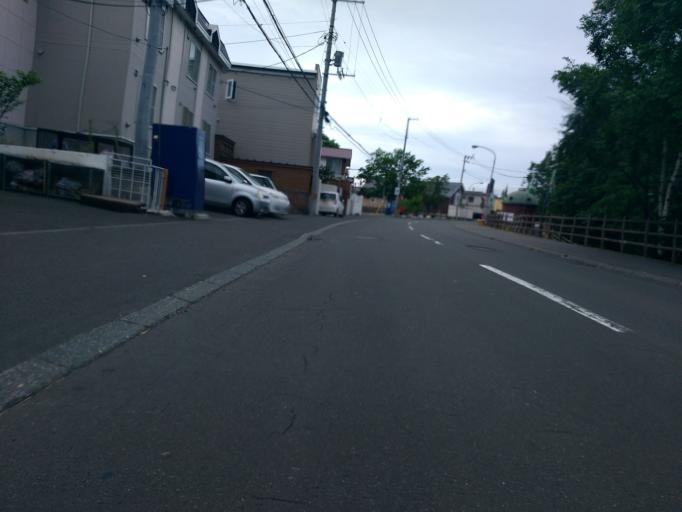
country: JP
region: Hokkaido
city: Ebetsu
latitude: 43.0663
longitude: 141.4984
